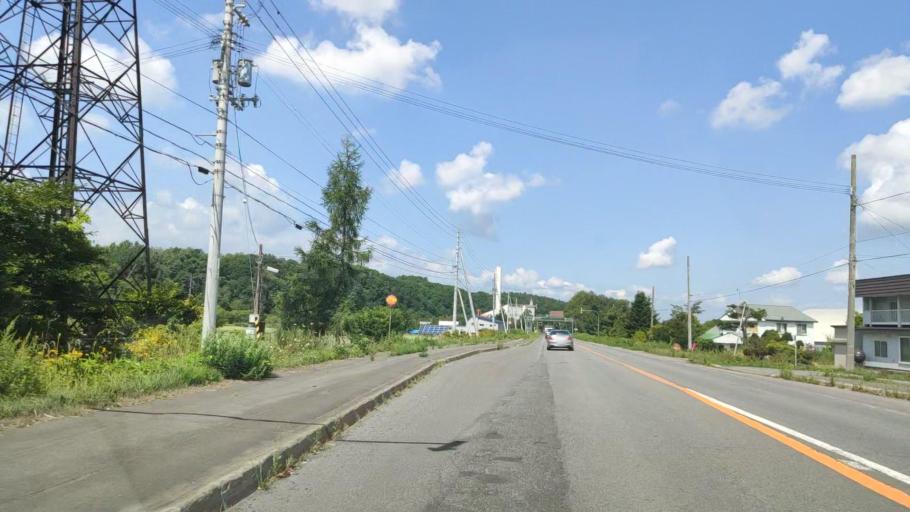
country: JP
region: Hokkaido
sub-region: Asahikawa-shi
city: Asahikawa
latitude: 43.6182
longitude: 142.4747
